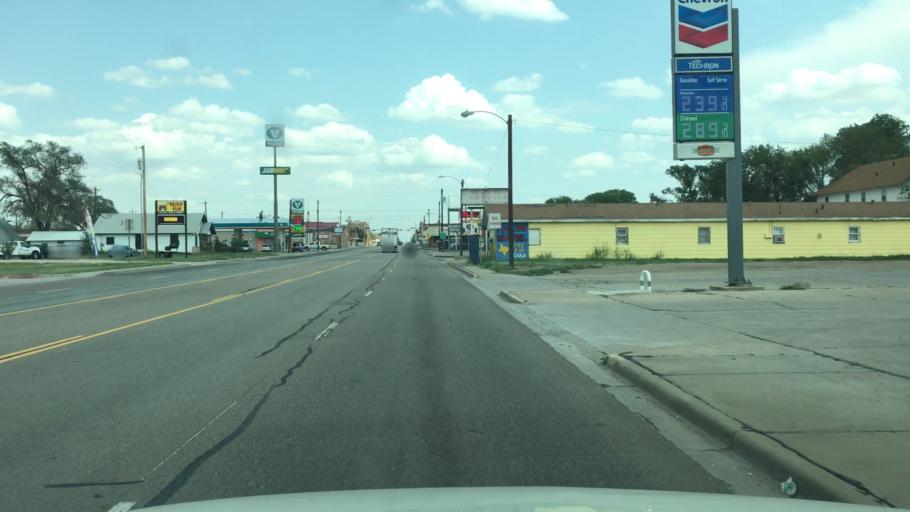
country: US
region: Texas
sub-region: Donley County
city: Clarendon
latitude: 34.9397
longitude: -100.8920
